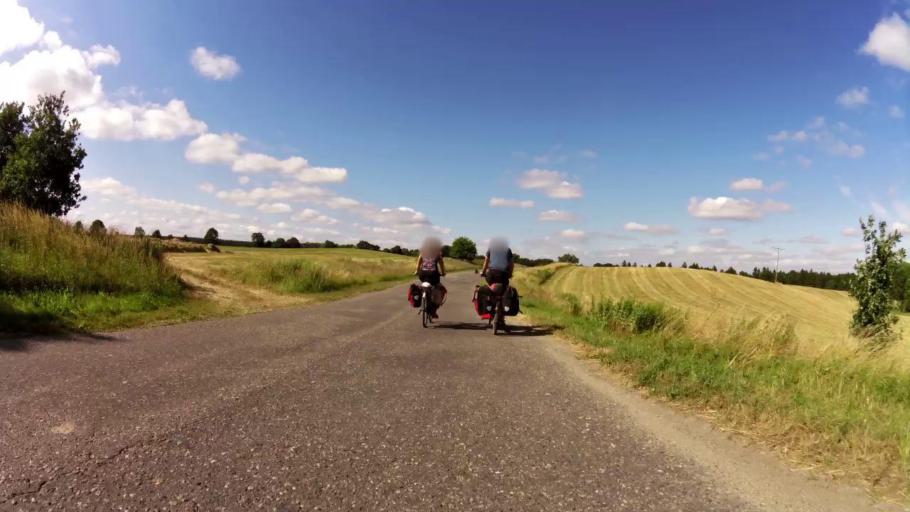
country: PL
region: West Pomeranian Voivodeship
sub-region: Powiat lobeski
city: Lobez
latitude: 53.6473
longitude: 15.6731
